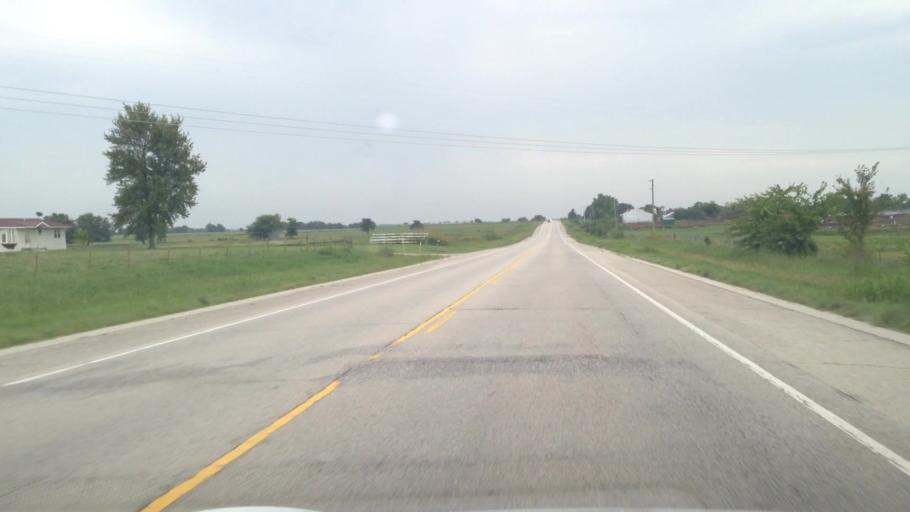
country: US
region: Oklahoma
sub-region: Ottawa County
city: Afton
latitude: 36.6632
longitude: -94.9814
